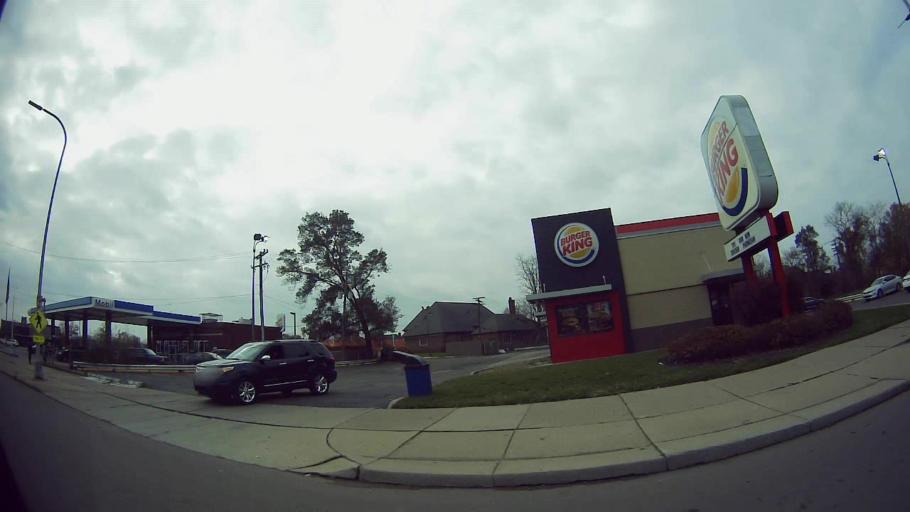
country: US
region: Michigan
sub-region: Wayne County
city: Highland Park
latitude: 42.3697
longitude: -83.1389
